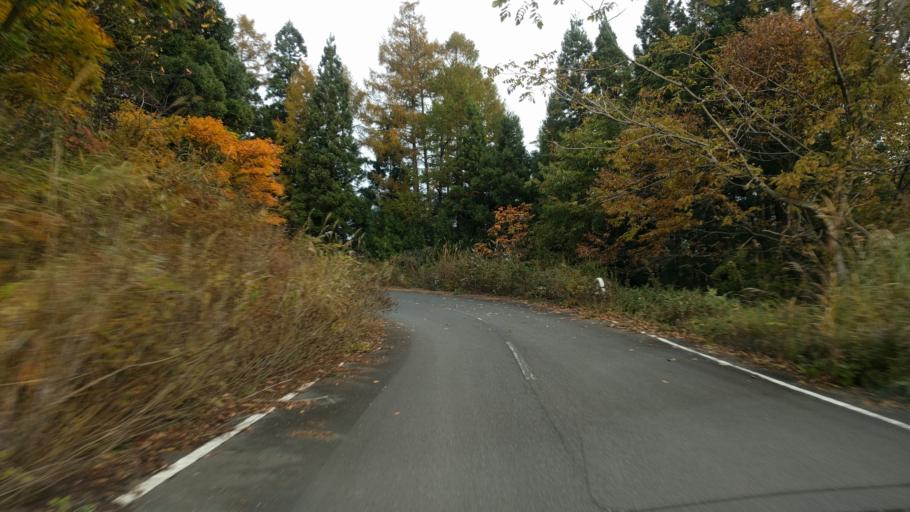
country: JP
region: Fukushima
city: Kitakata
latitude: 37.3923
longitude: 139.7373
